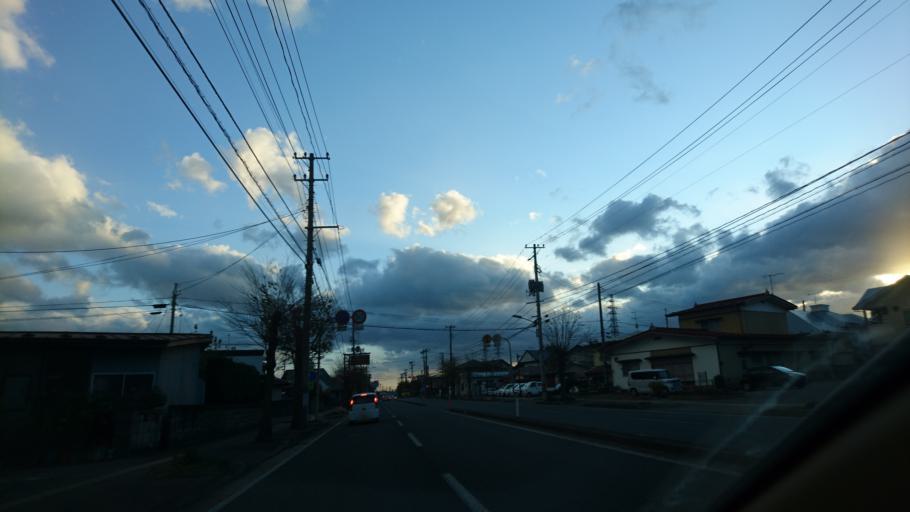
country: JP
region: Iwate
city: Mizusawa
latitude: 39.1452
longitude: 141.1300
